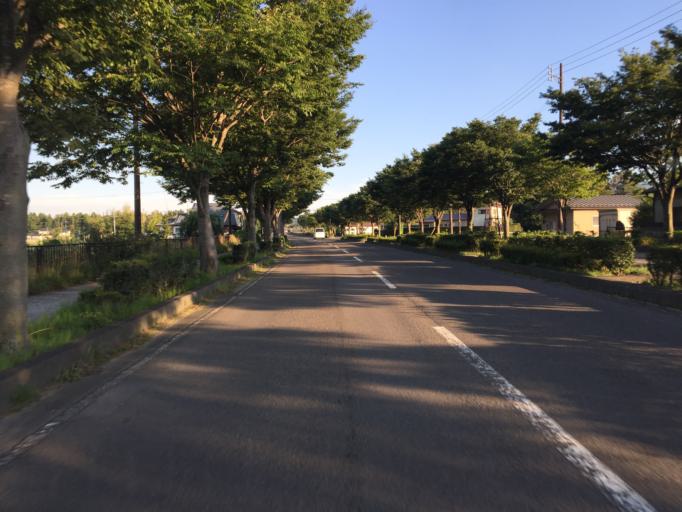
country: JP
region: Fukushima
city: Fukushima-shi
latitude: 37.7406
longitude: 140.3830
